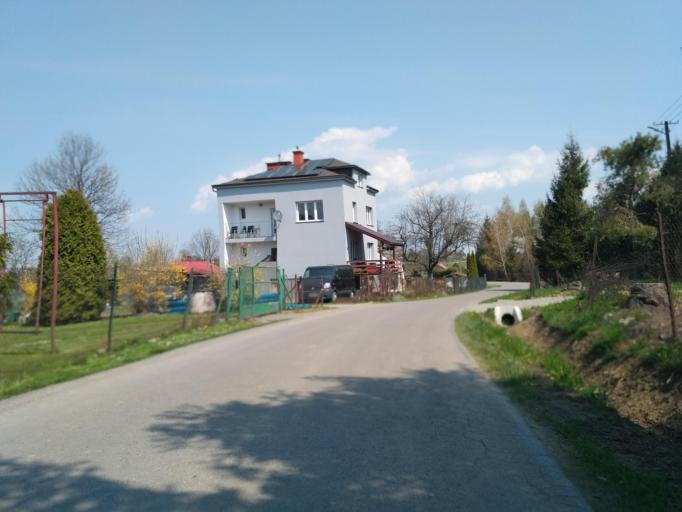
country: PL
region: Subcarpathian Voivodeship
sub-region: Powiat krosnienski
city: Chorkowka
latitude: 49.6259
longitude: 21.7036
